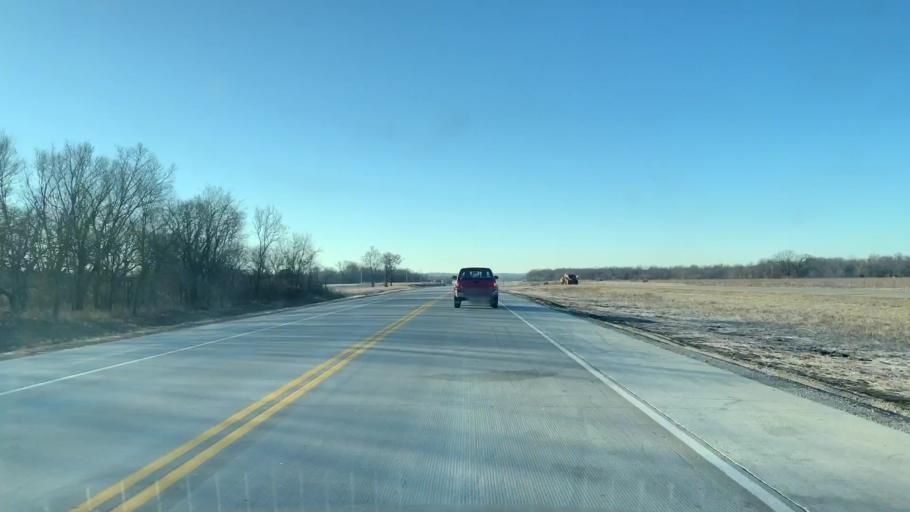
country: US
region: Kansas
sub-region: Bourbon County
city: Fort Scott
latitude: 37.7204
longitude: -94.7042
